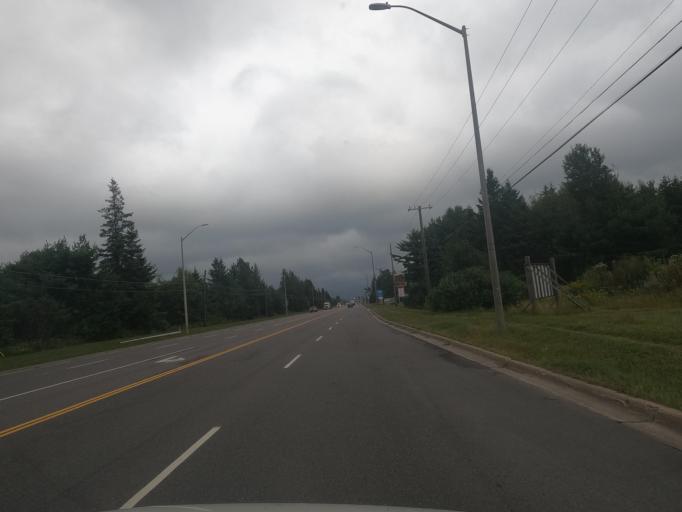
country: CA
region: Ontario
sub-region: Algoma
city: Sault Ste. Marie
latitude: 46.5354
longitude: -84.2427
